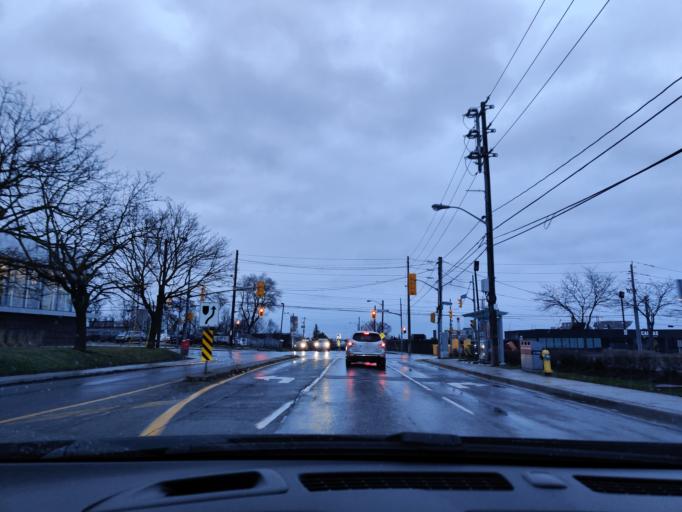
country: CA
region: Ontario
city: Toronto
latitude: 43.6990
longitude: -79.4637
